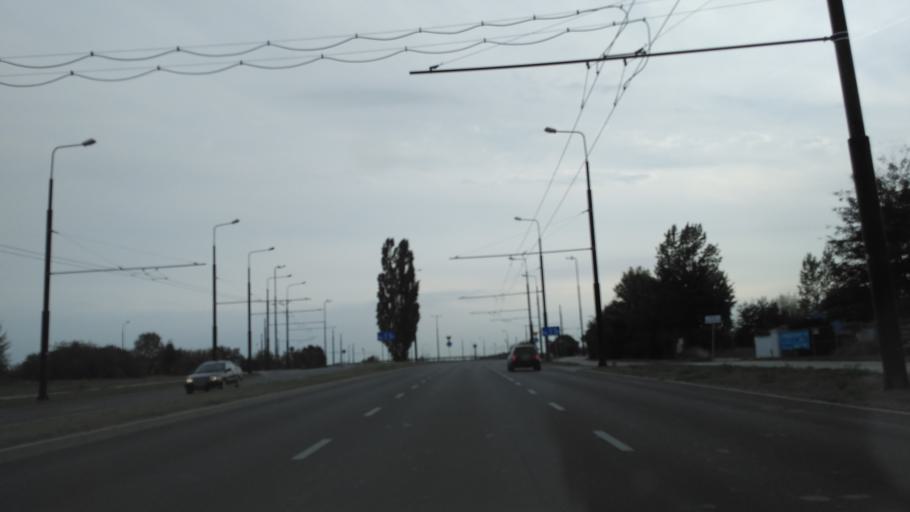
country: PL
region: Lublin Voivodeship
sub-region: Powiat lubelski
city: Jakubowice Murowane
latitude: 51.2296
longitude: 22.6209
